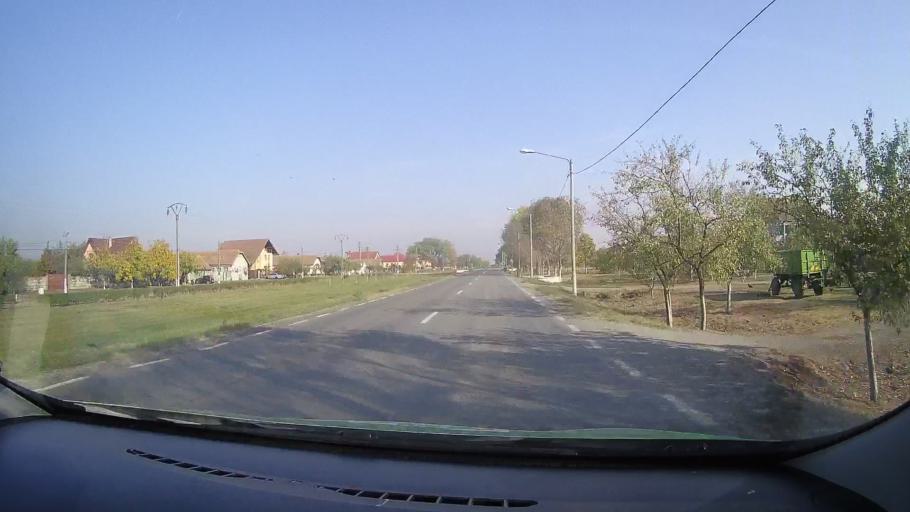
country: RO
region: Arad
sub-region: Comuna Pilu
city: Pilu
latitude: 46.5739
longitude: 21.3424
